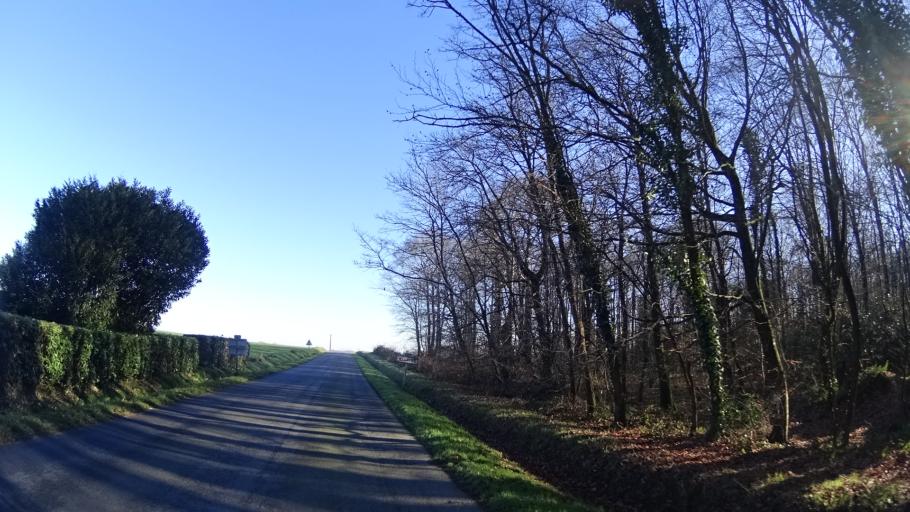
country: FR
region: Brittany
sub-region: Departement du Morbihan
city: Allaire
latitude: 47.6407
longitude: -2.1563
